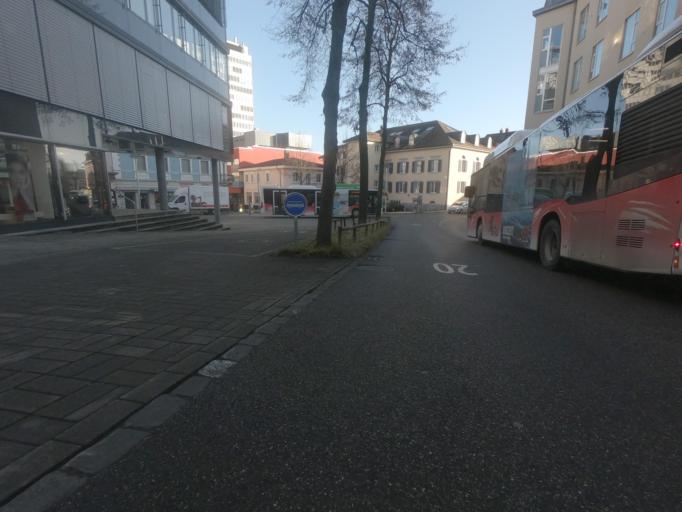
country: CH
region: Solothurn
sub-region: Bezirk Lebern
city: Grenchen
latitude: 47.1929
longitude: 7.3955
